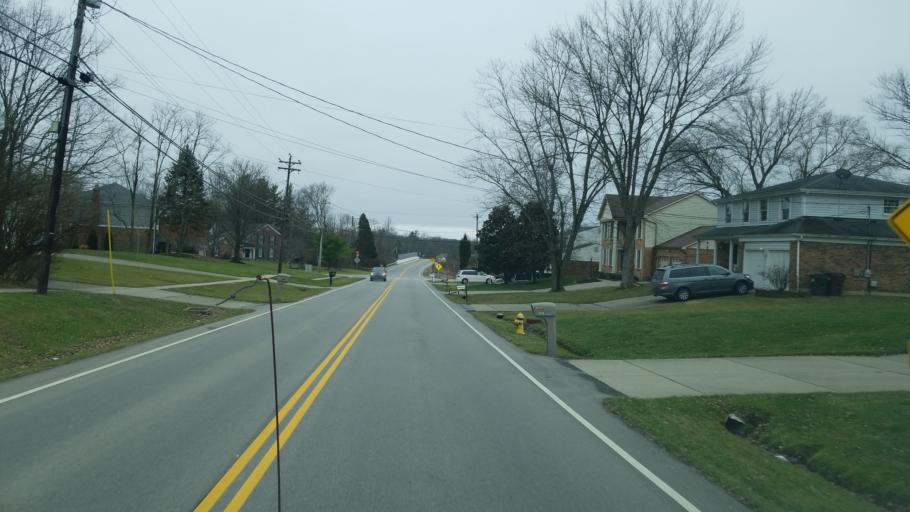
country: US
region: Ohio
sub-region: Hamilton County
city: Cherry Grove
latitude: 39.0602
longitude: -84.3249
